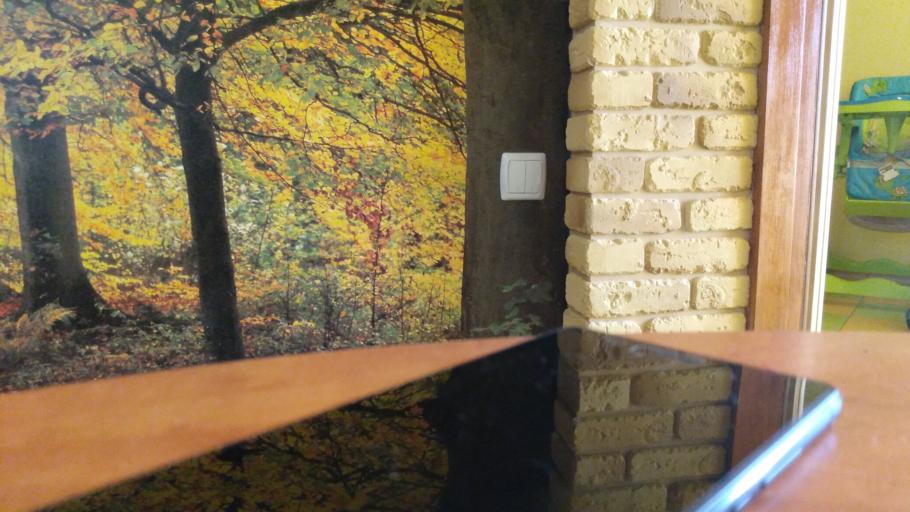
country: RU
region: Tverskaya
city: Vyshniy Volochek
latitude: 57.6946
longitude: 34.6264
